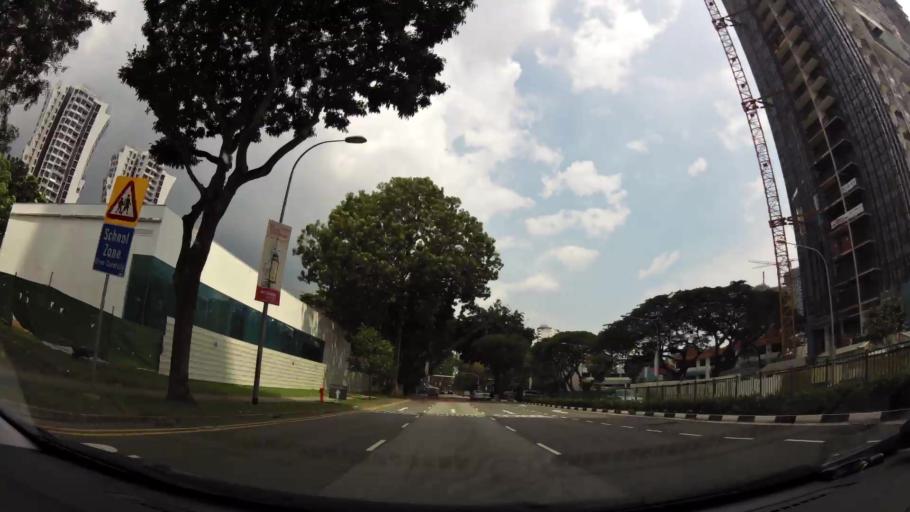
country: SG
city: Singapore
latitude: 1.2912
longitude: 103.8188
